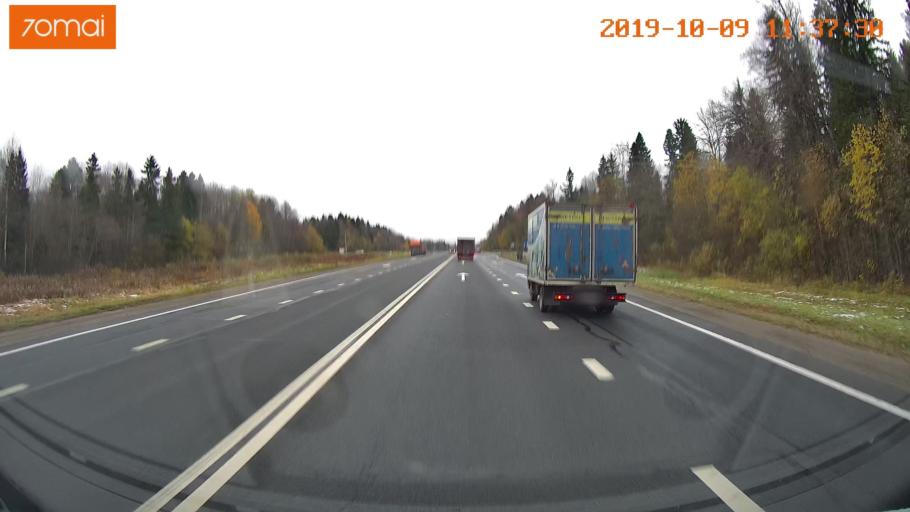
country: RU
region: Vologda
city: Gryazovets
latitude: 58.9786
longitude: 40.1470
